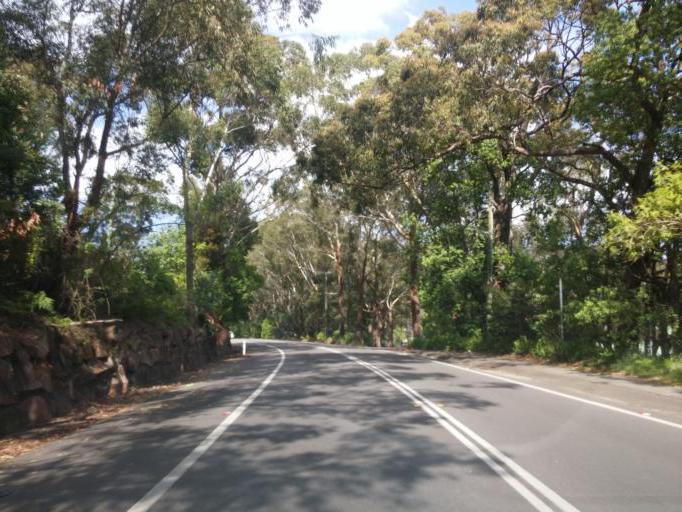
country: AU
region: New South Wales
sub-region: Port Stephens Shire
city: Nelson Bay
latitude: -32.7258
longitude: 152.1390
